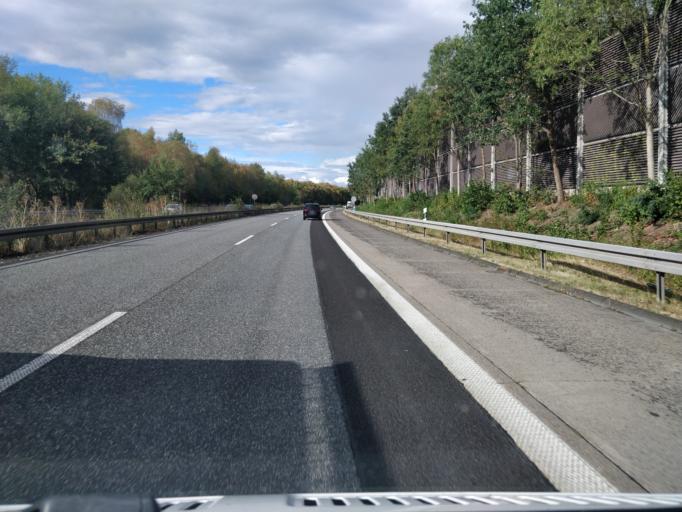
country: DE
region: North Rhine-Westphalia
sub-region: Regierungsbezirk Koln
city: Bonn
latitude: 50.6903
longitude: 7.0576
